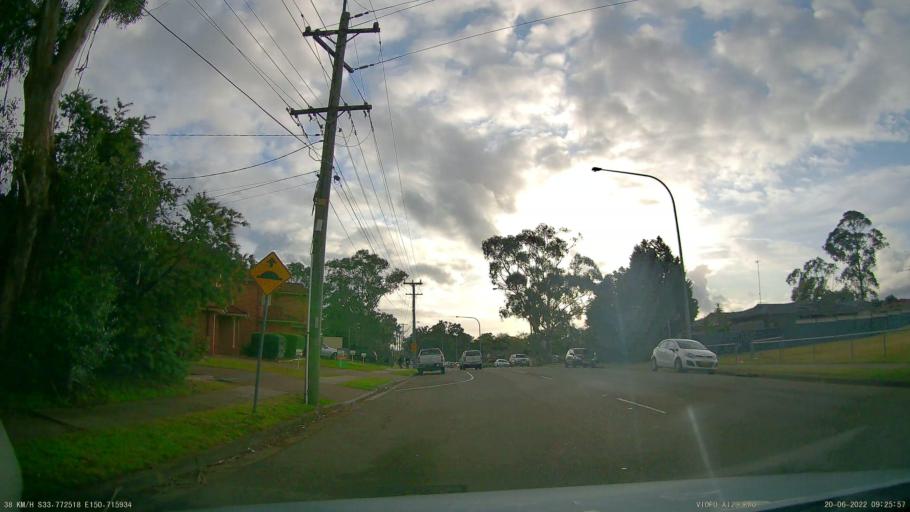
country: AU
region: New South Wales
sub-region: Penrith Municipality
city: Kingswood Park
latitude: -33.7724
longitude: 150.7160
